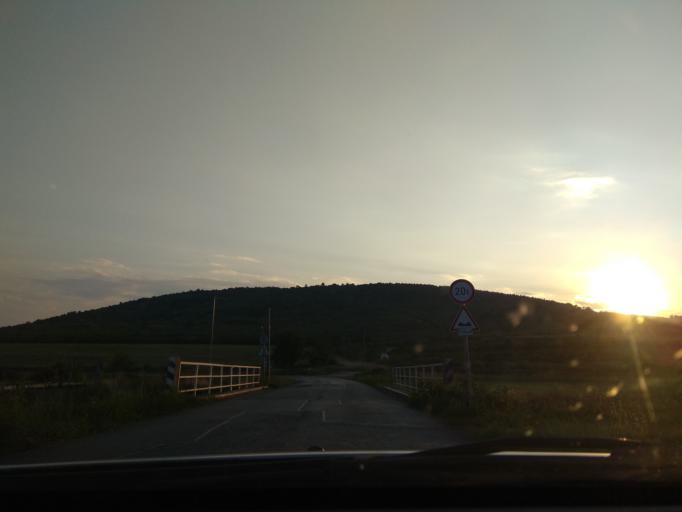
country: HU
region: Borsod-Abauj-Zemplen
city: Tallya
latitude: 48.2057
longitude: 21.2127
